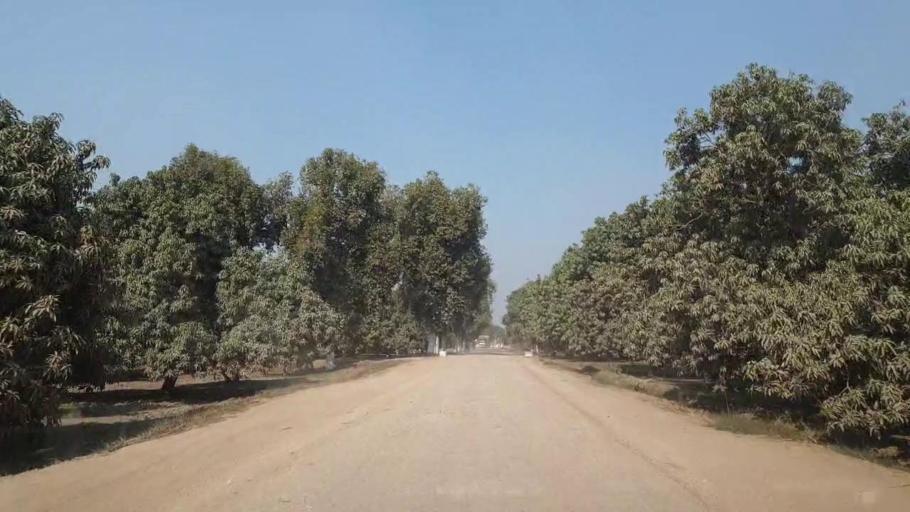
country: PK
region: Sindh
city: Tando Allahyar
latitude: 25.4882
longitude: 68.8226
